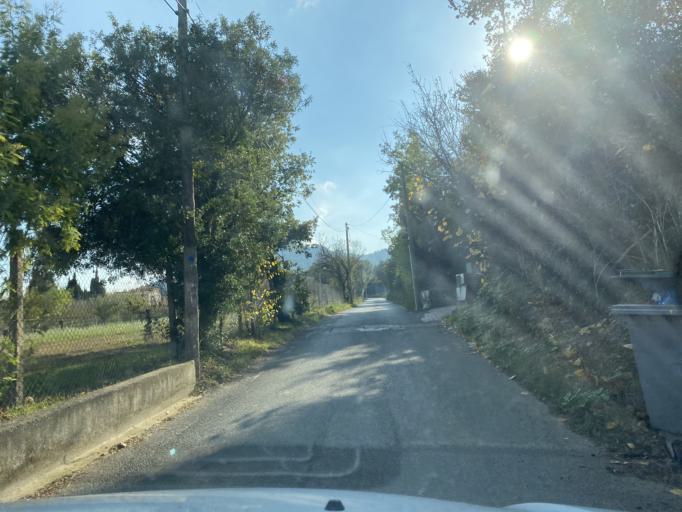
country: FR
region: Provence-Alpes-Cote d'Azur
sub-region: Departement du Var
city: Six-Fours-les-Plages
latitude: 43.1141
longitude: 5.8392
